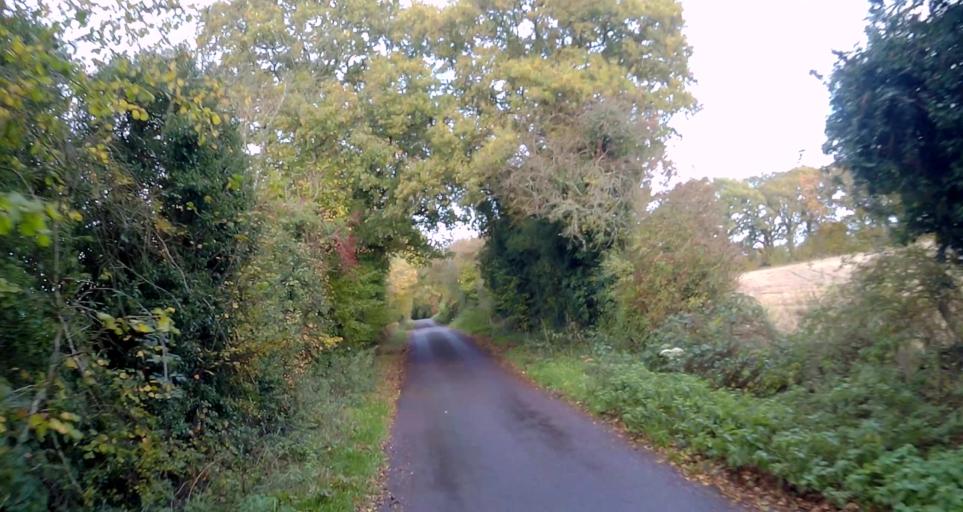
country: GB
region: England
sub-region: Hampshire
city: Four Marks
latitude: 51.1489
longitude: -1.0905
